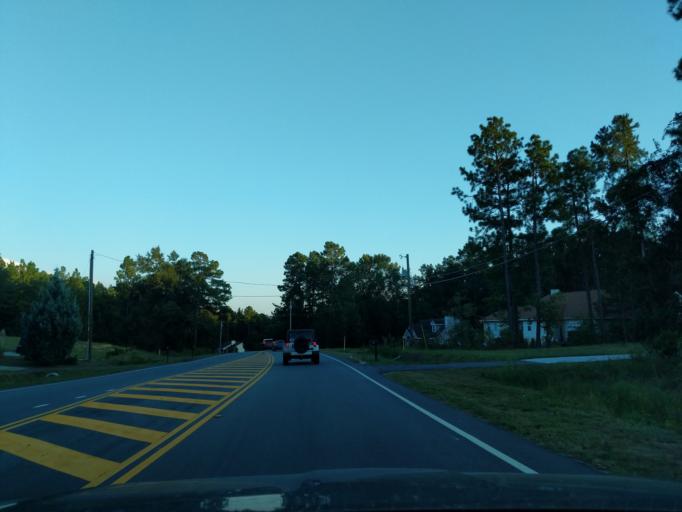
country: US
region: South Carolina
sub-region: Aiken County
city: Burnettown
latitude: 33.5321
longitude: -81.8602
